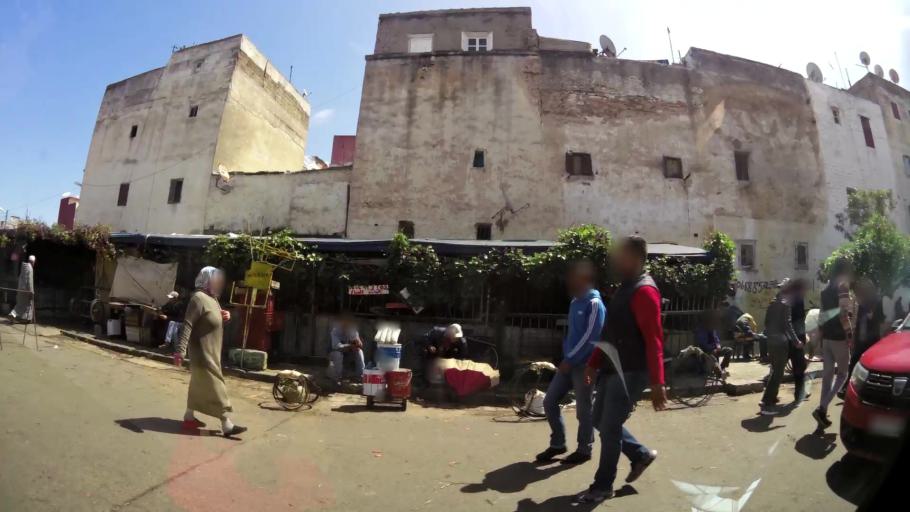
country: MA
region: Grand Casablanca
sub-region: Casablanca
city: Casablanca
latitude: 33.5978
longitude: -7.6243
